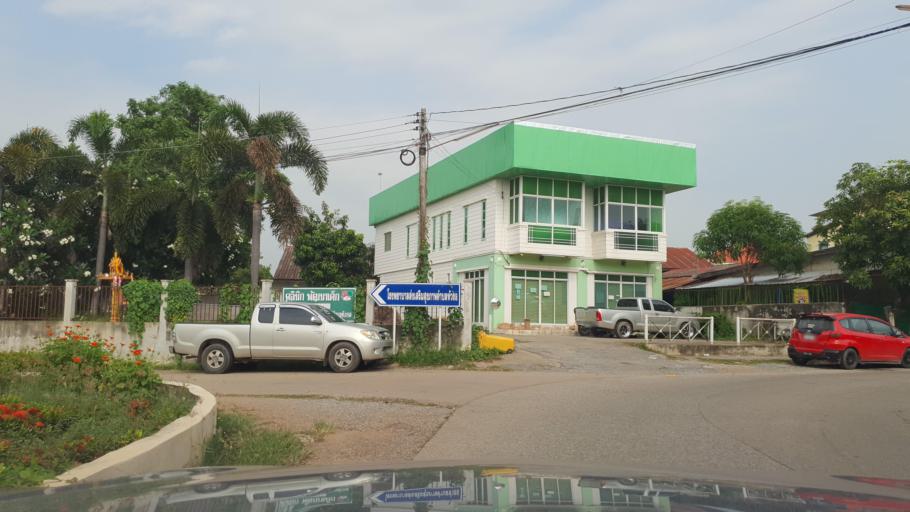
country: TH
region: Phitsanulok
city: Phitsanulok
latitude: 16.8497
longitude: 100.2555
